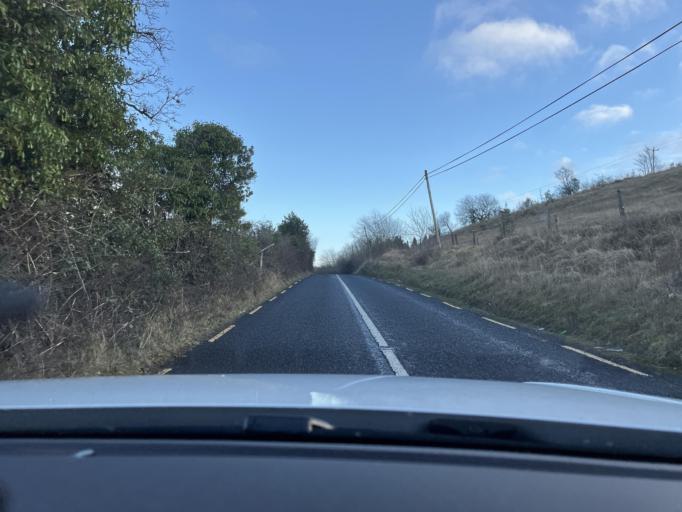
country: IE
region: Connaught
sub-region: County Leitrim
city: Manorhamilton
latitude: 54.1994
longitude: -7.9438
